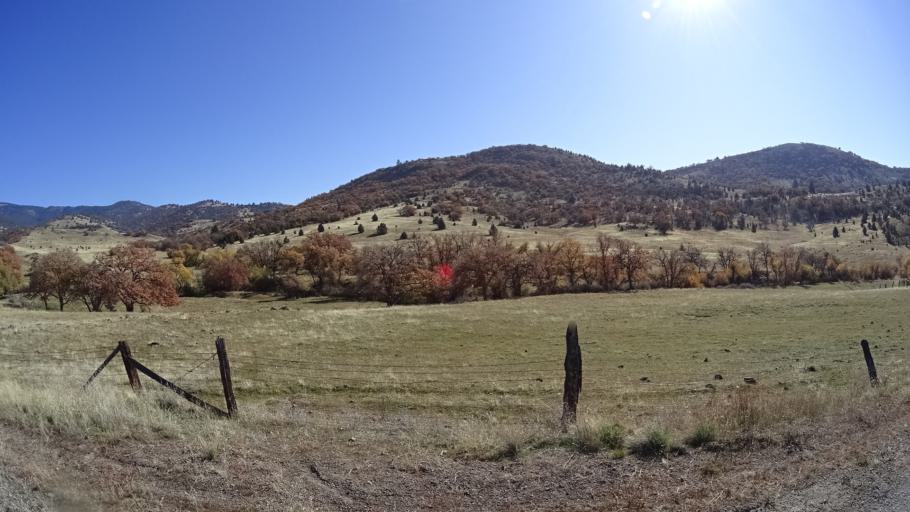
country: US
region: California
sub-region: Siskiyou County
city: Montague
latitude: 41.7953
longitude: -122.3377
